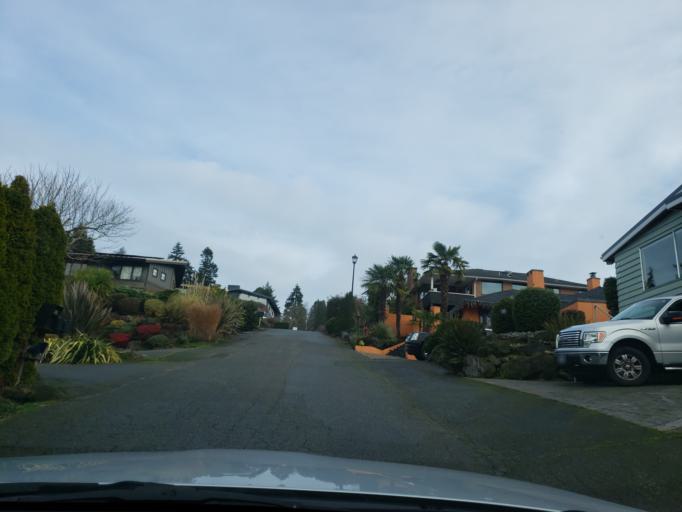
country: US
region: Washington
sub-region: King County
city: Shoreline
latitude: 47.7016
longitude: -122.3862
